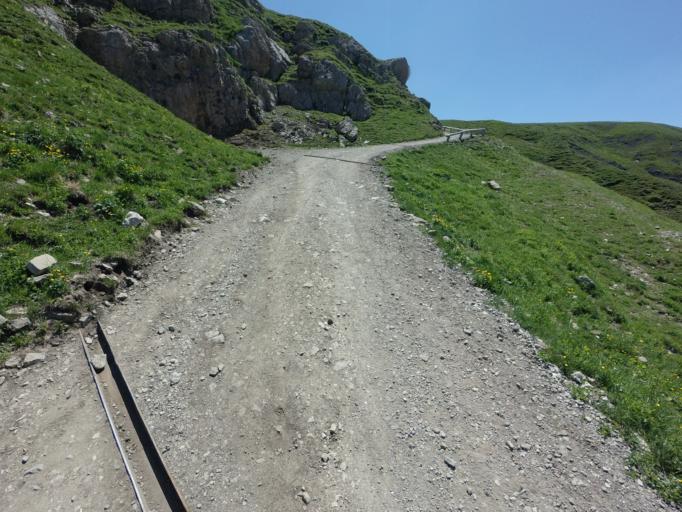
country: IT
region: Trentino-Alto Adige
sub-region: Provincia di Trento
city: Mazzin
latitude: 46.5066
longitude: 11.6982
